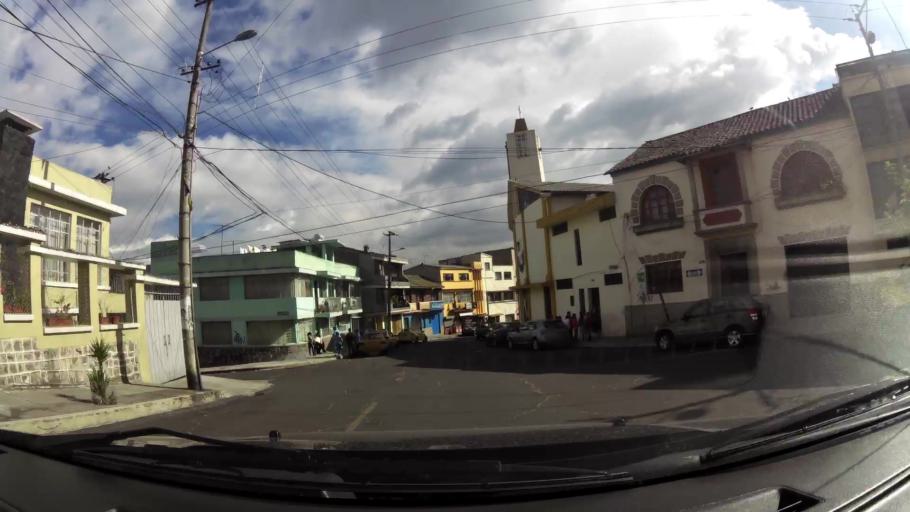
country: EC
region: Pichincha
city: Quito
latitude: -0.2275
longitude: -78.5036
